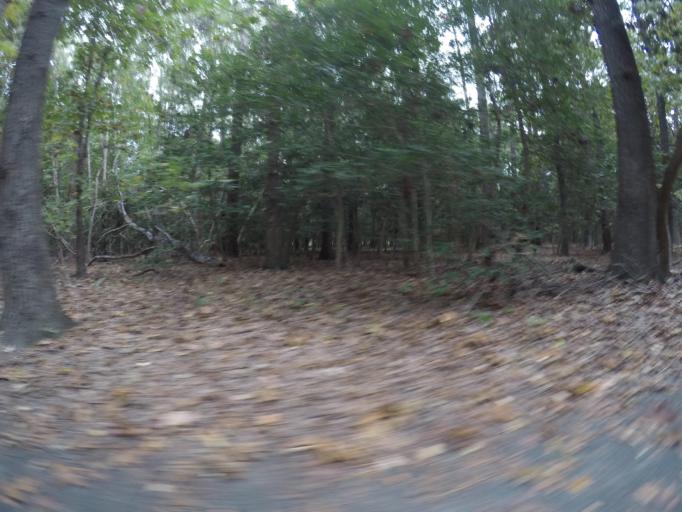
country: US
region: Delaware
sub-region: Sussex County
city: Rehoboth Beach
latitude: 38.7188
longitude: -75.1054
